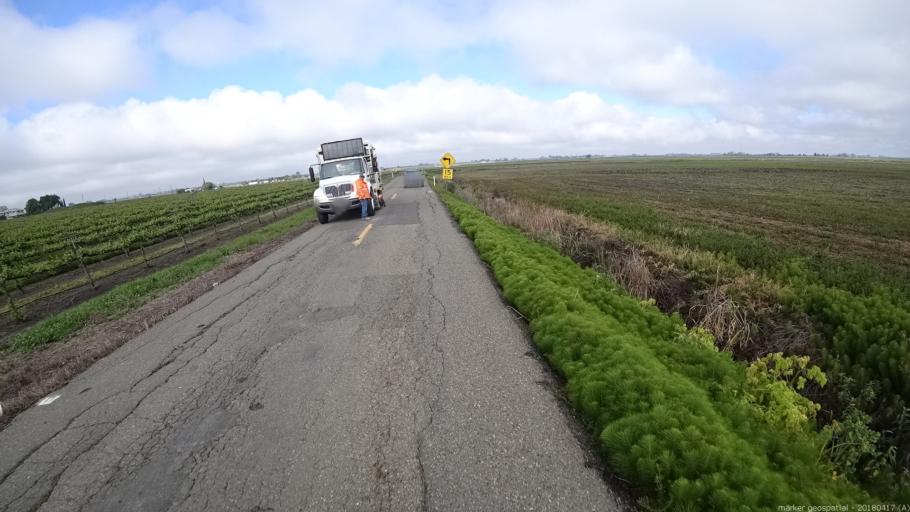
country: US
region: California
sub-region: Sacramento County
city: Walnut Grove
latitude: 38.2136
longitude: -121.5656
